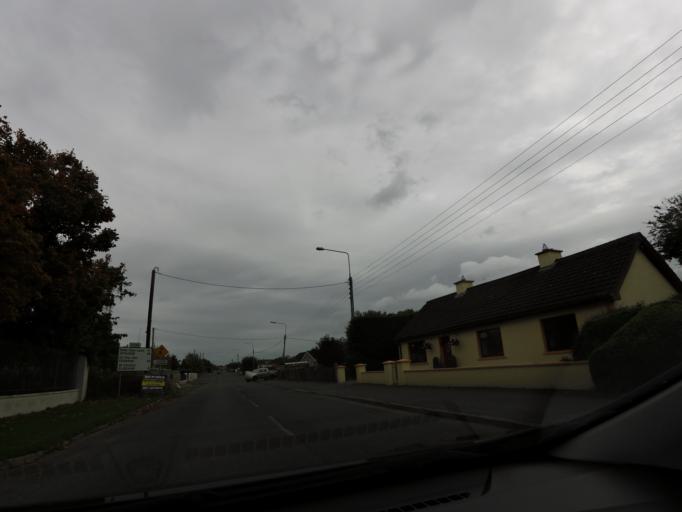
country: IE
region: Leinster
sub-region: Uibh Fhaili
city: Banagher
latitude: 53.1926
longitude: -7.9809
